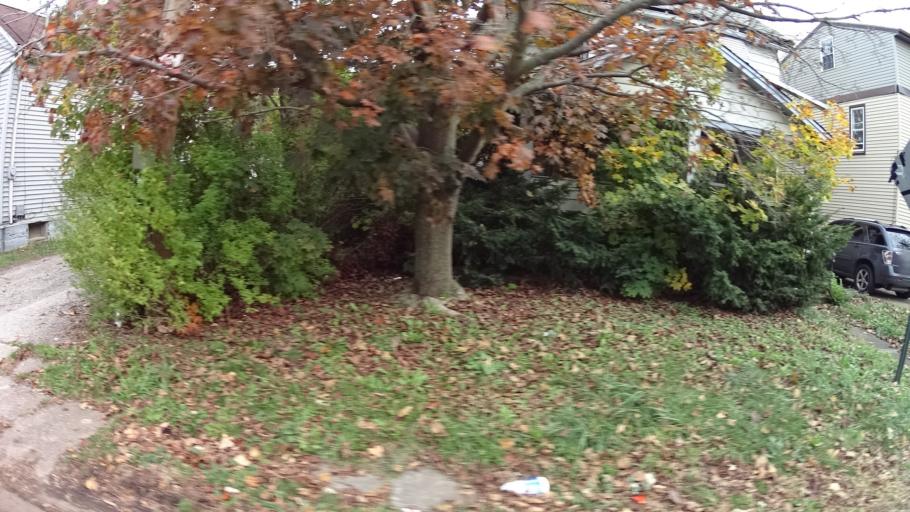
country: US
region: Ohio
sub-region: Lorain County
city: Lorain
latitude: 41.4741
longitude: -82.1606
